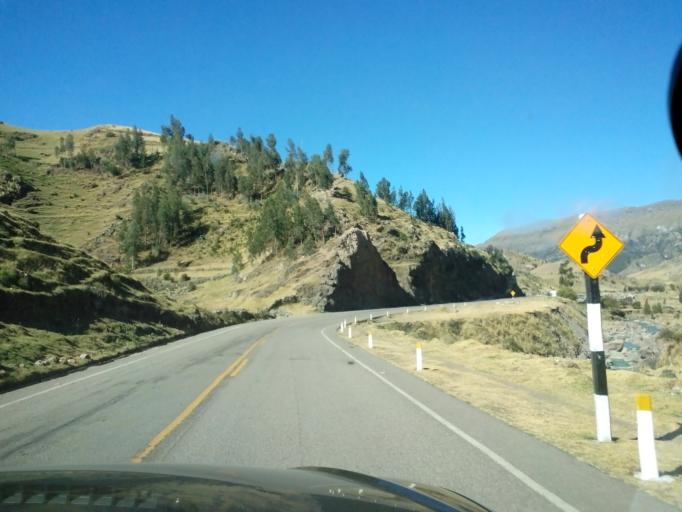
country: PE
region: Ayacucho
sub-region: Provincia de Huamanga
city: Vinchos
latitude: -13.3429
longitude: -74.4890
